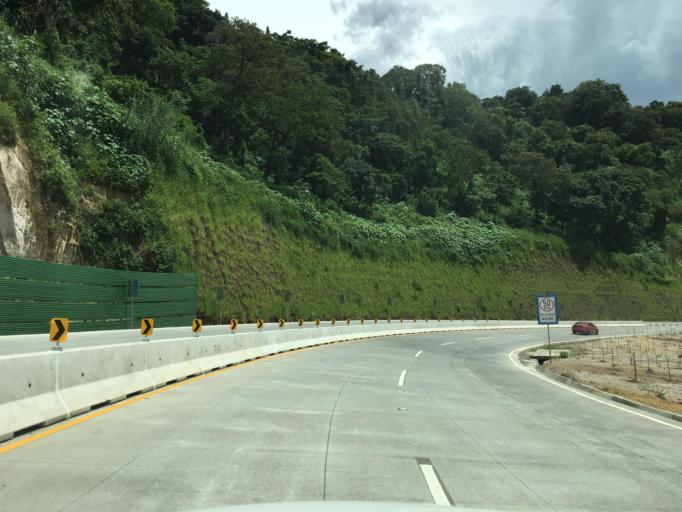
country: GT
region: Guatemala
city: Santa Catarina Pinula
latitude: 14.5564
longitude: -90.5328
